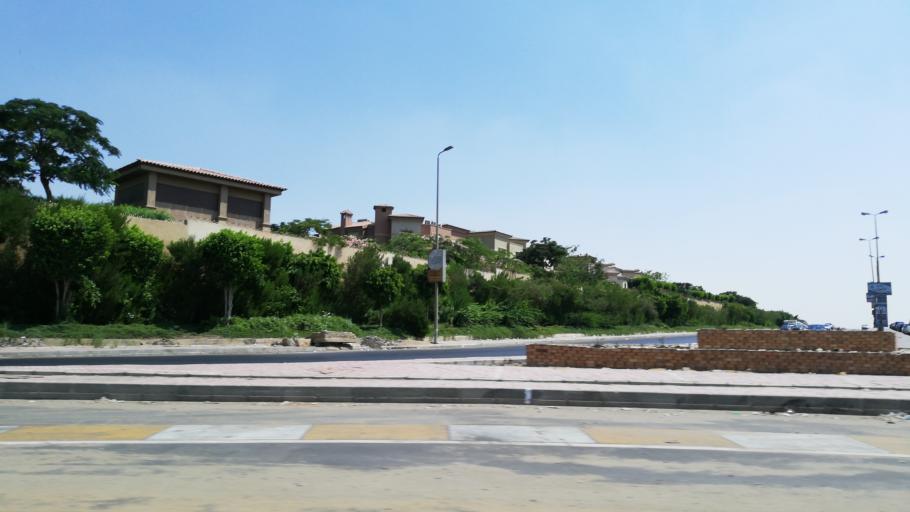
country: EG
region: Muhafazat al Qahirah
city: Cairo
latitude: 30.0214
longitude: 31.4365
